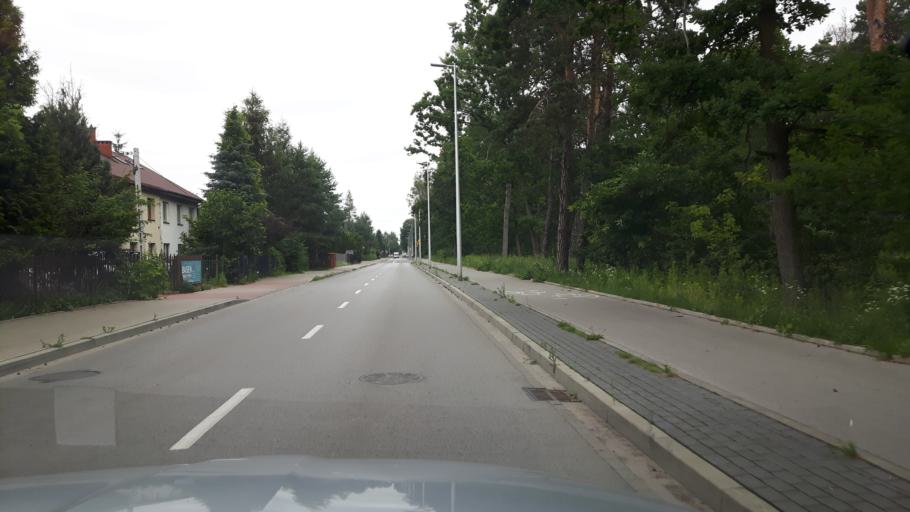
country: PL
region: Masovian Voivodeship
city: Zielonka
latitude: 52.2927
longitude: 21.1632
